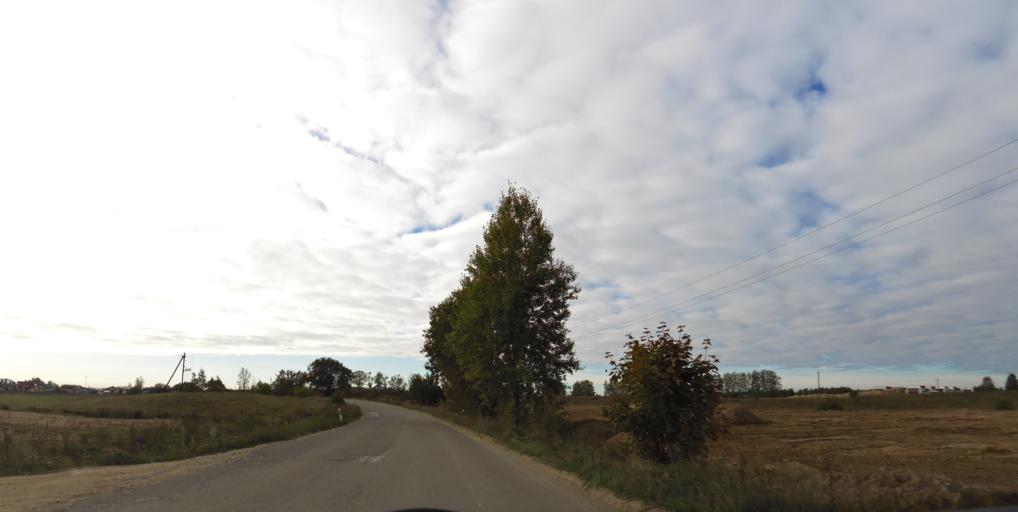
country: LT
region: Vilnius County
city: Pilaite
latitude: 54.7262
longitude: 25.1526
